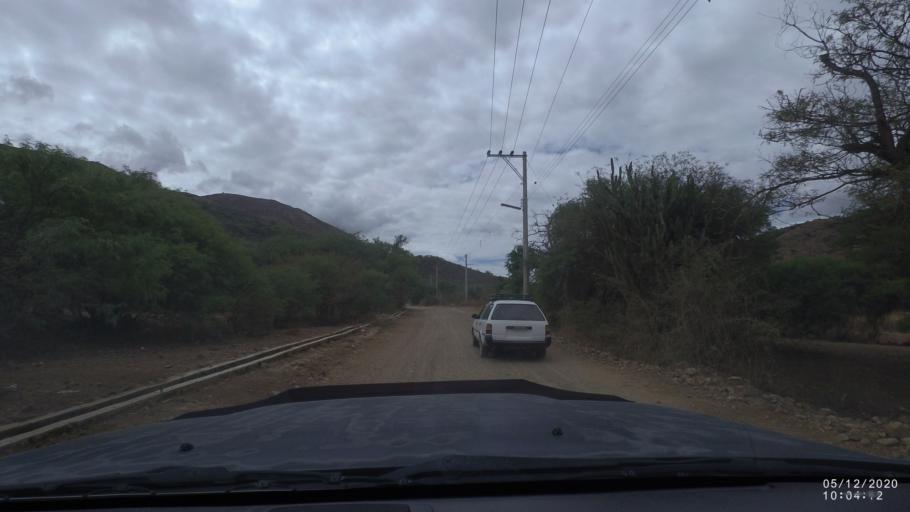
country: BO
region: Cochabamba
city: Sipe Sipe
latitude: -17.4617
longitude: -66.2866
